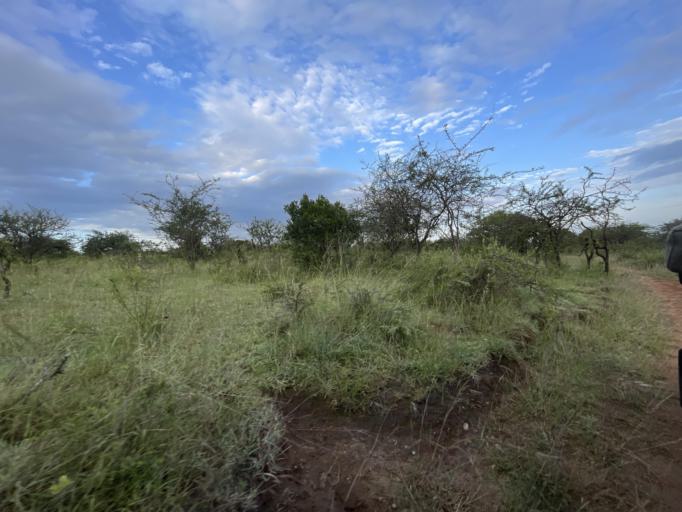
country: TZ
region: Mara
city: Mugumu
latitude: -1.7027
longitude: 35.3077
